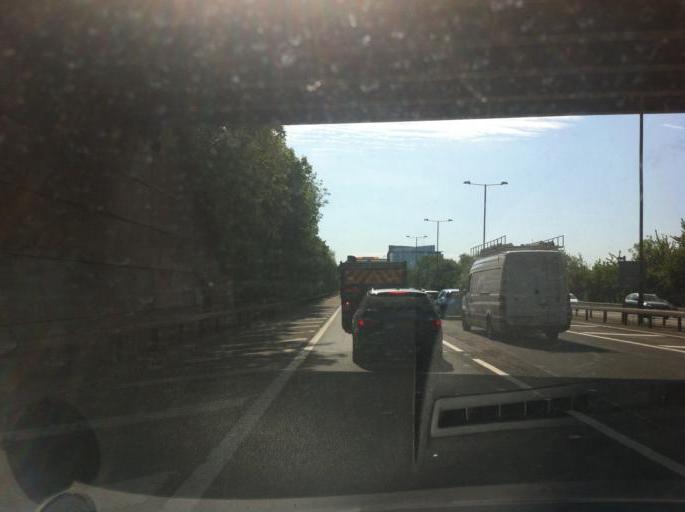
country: GB
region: England
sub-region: Greater London
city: Brentford
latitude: 51.4940
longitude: -0.3278
